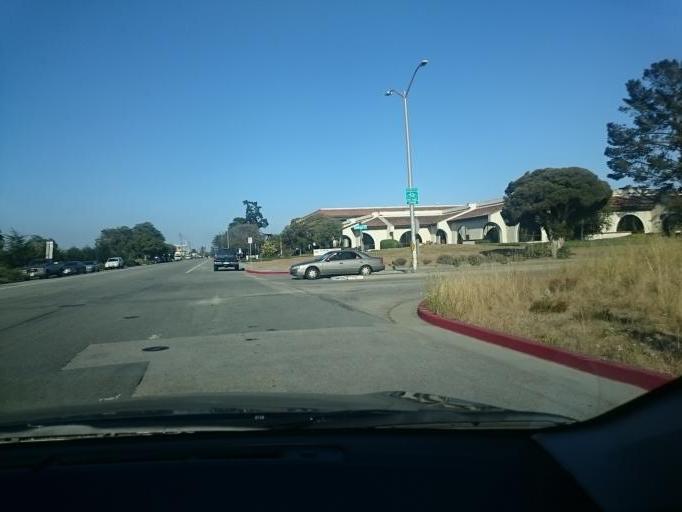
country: US
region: California
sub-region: Santa Cruz County
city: Santa Cruz
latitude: 36.9549
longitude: -122.0553
